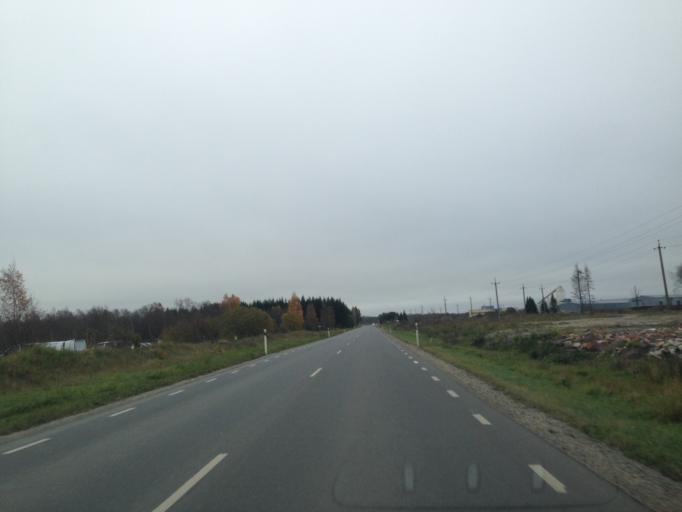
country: EE
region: Harju
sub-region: Harku vald
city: Tabasalu
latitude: 59.4119
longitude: 24.5453
